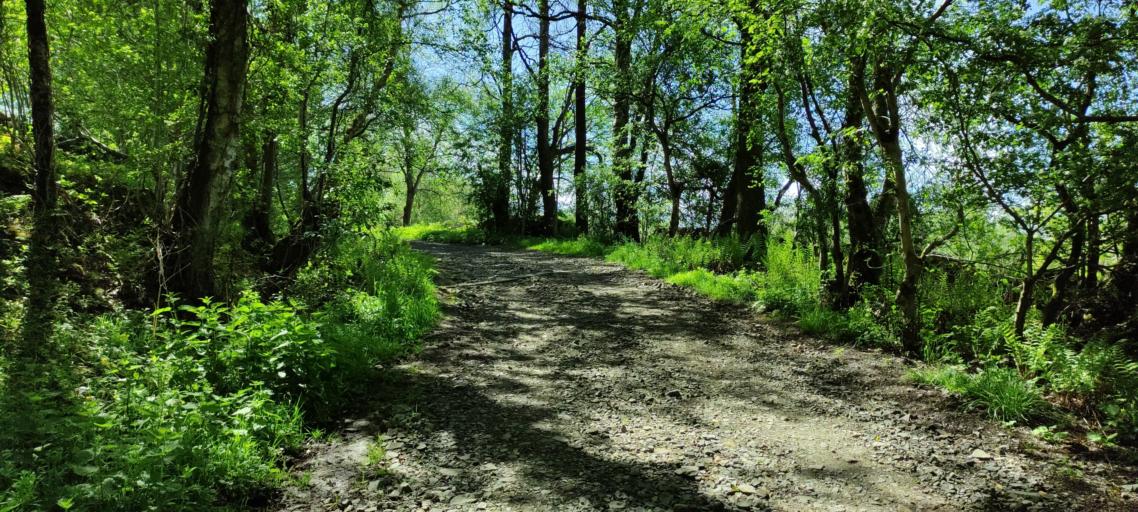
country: GB
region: England
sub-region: Cumbria
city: Brampton
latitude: 54.8941
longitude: -2.6888
